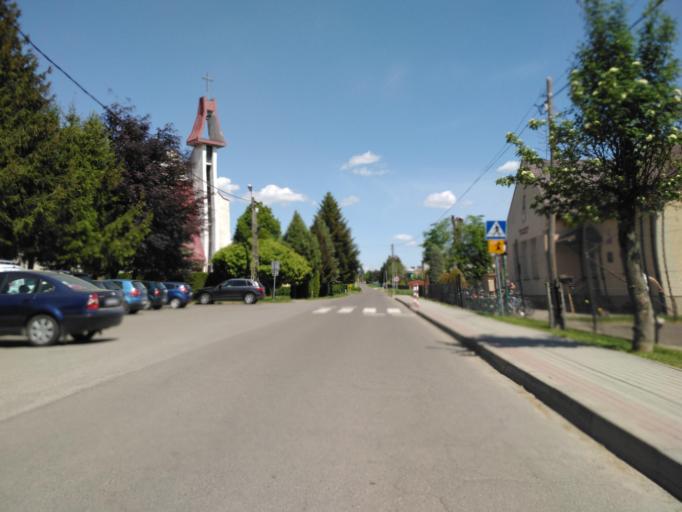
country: PL
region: Subcarpathian Voivodeship
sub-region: Powiat krosnienski
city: Jedlicze
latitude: 49.6982
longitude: 21.6791
